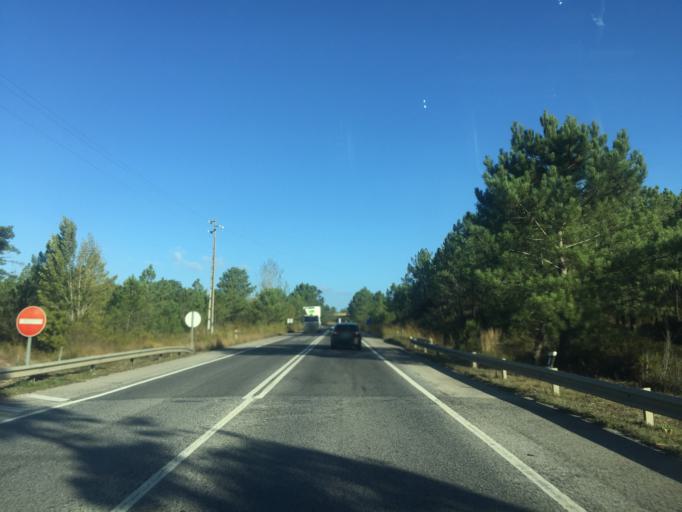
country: PT
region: Lisbon
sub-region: Azambuja
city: Alcoentre
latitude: 39.2217
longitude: -8.9547
